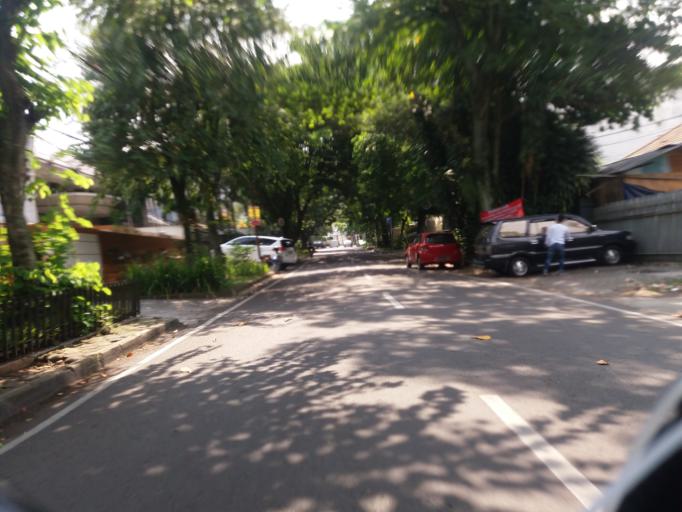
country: ID
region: West Java
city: Bandung
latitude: -6.9019
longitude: 107.6135
